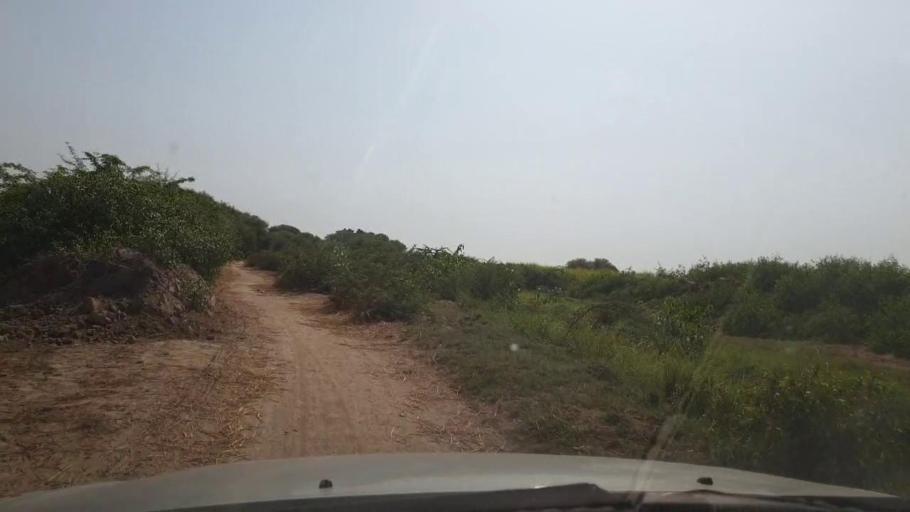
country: PK
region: Sindh
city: Bulri
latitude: 24.8700
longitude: 68.3108
